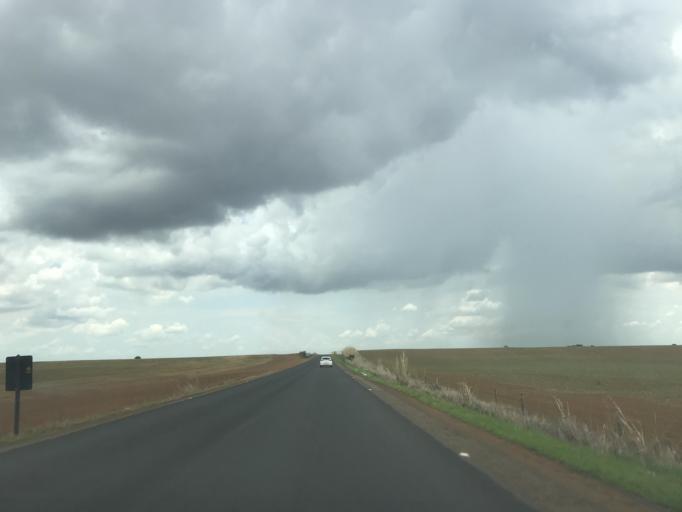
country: BR
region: Goias
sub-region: Vianopolis
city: Vianopolis
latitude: -16.8509
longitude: -48.5377
